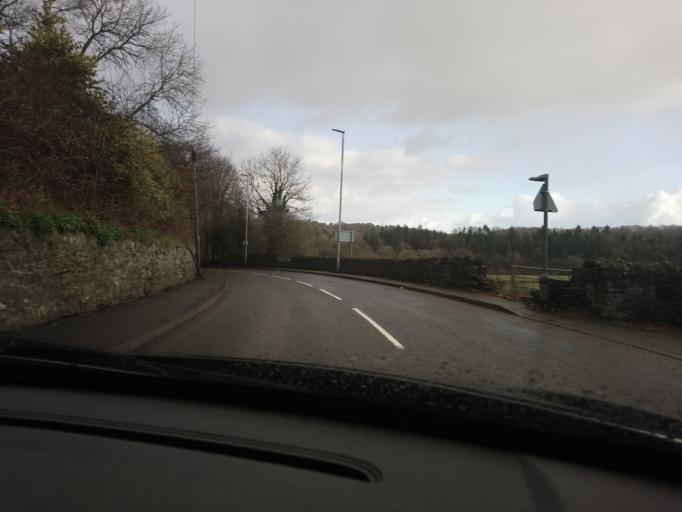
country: GB
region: Wales
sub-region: Wrexham
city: Chirk
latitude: 52.9661
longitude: -3.0655
